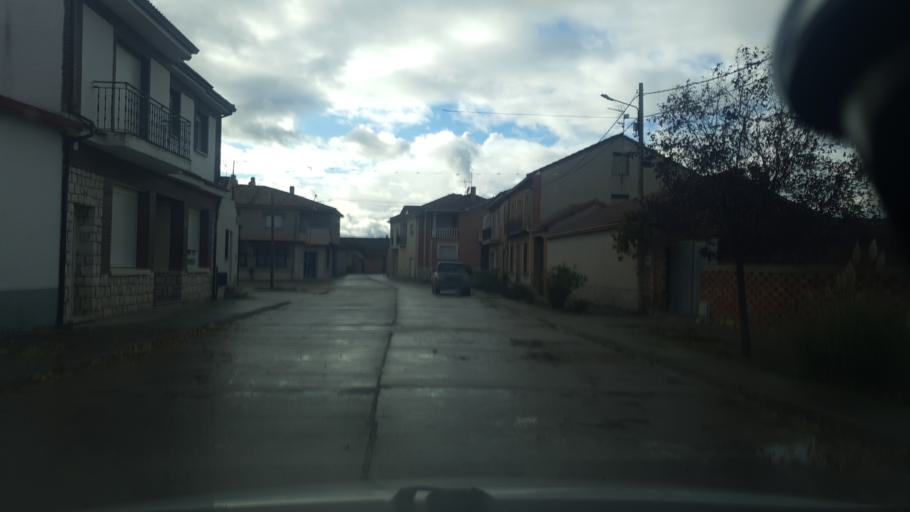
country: ES
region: Castille and Leon
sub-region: Provincia de Segovia
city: Sanchonuno
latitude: 41.2896
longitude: -4.3247
